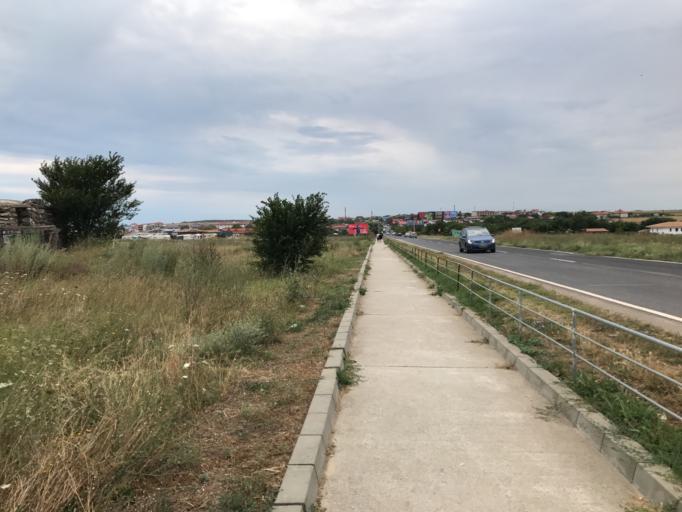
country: RO
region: Constanta
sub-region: Municipiul Mangalia
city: Mangalia
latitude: 43.7599
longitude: 28.5730
